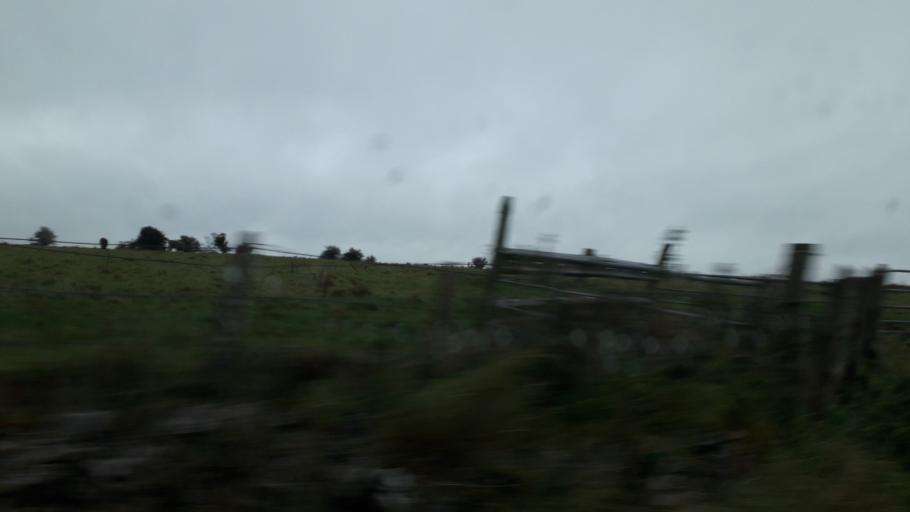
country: IE
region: Connaught
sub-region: Roscommon
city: Roscommon
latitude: 53.7674
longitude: -8.2066
